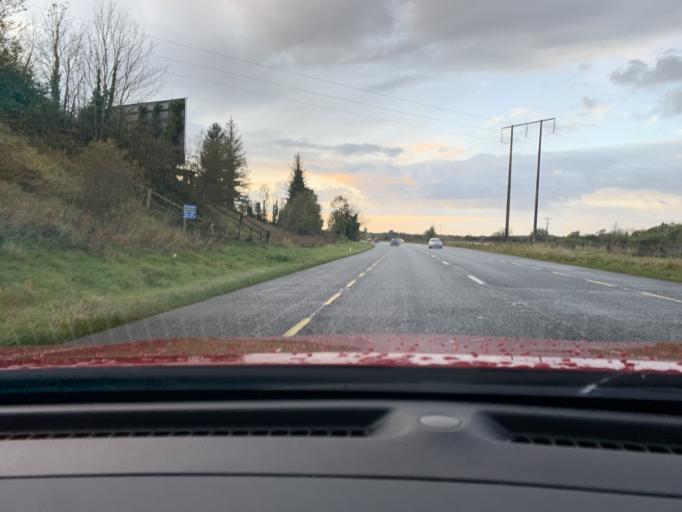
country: IE
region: Connaught
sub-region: County Leitrim
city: Carrick-on-Shannon
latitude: 53.9470
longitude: -8.1218
